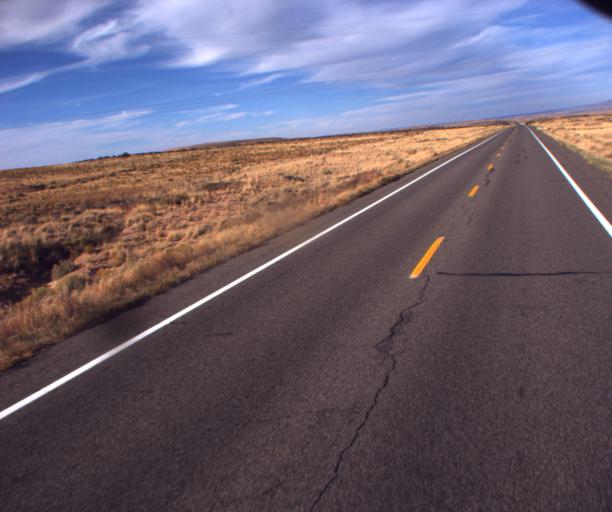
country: US
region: Colorado
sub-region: Montezuma County
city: Towaoc
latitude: 36.9598
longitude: -109.0668
